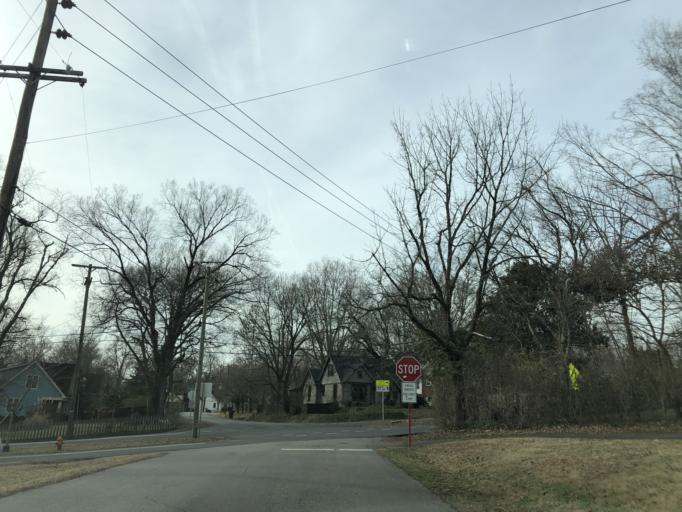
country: US
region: Tennessee
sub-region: Davidson County
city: Nashville
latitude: 36.2086
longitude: -86.7232
